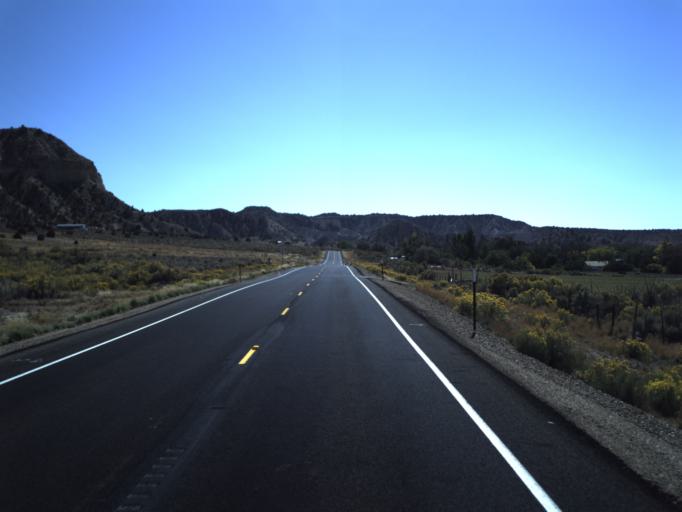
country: US
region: Utah
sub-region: Garfield County
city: Panguitch
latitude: 37.5690
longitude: -111.9896
